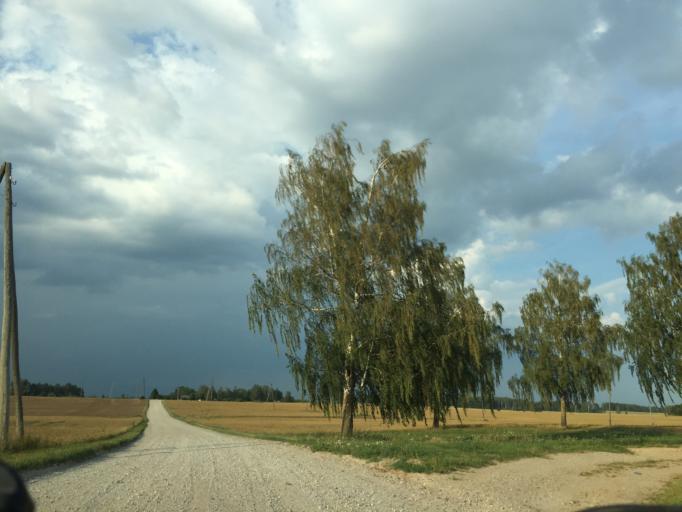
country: LV
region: Dobeles Rajons
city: Dobele
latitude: 56.5842
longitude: 23.3032
